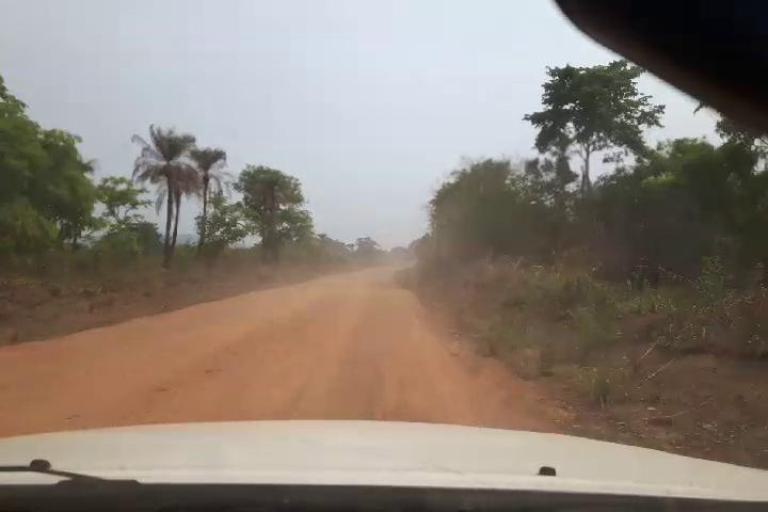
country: SL
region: Northern Province
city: Masingbi
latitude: 8.8835
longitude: -11.8196
